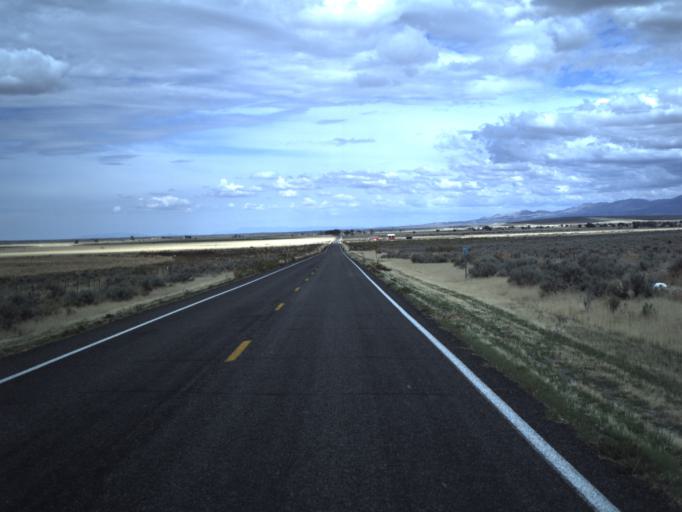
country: US
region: Utah
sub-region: Millard County
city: Fillmore
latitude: 39.0122
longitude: -112.4099
